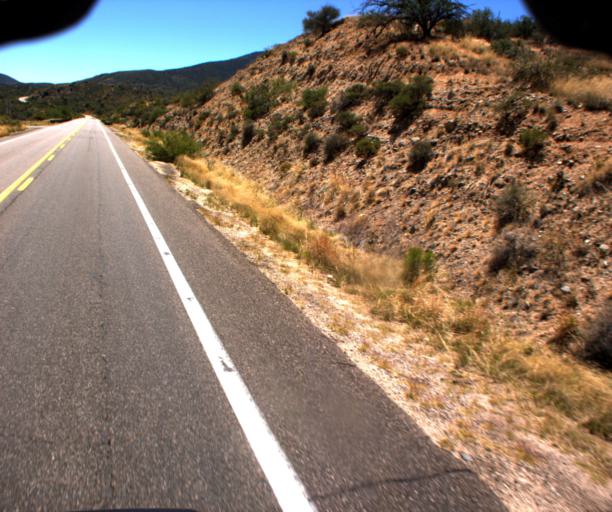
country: US
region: Arizona
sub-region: Gila County
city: Globe
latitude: 33.3225
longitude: -110.7333
